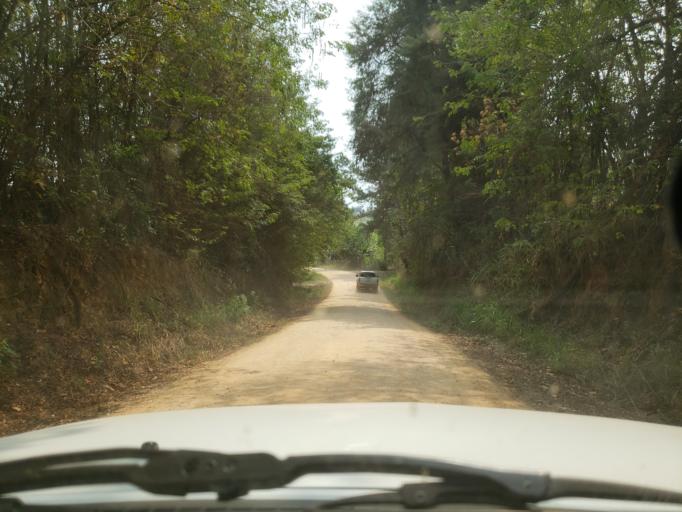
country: BR
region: Minas Gerais
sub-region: Jacutinga
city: Jacutinga
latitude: -22.3149
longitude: -46.6030
